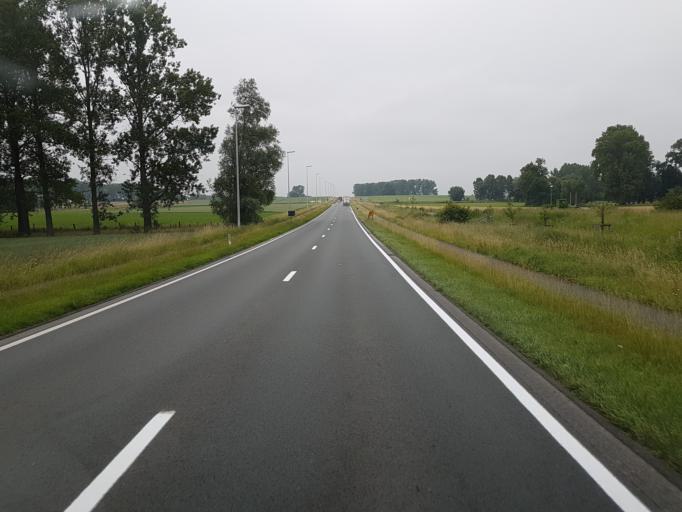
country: BE
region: Flanders
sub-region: Provincie Oost-Vlaanderen
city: Sint-Maria-Lierde
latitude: 50.8150
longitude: 3.8705
